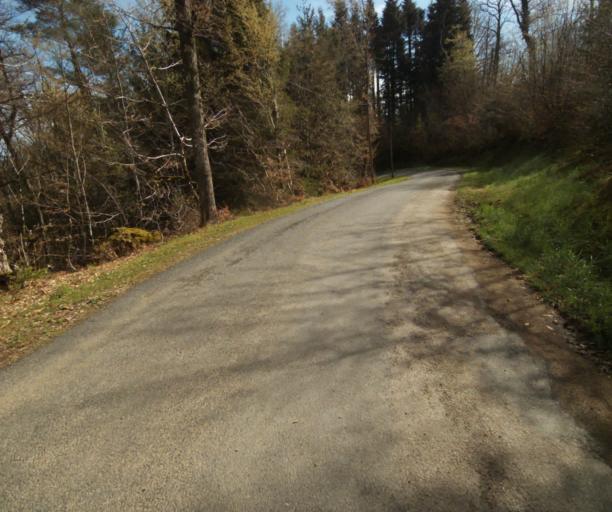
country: FR
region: Limousin
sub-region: Departement de la Correze
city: Laguenne
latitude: 45.2816
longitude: 1.8296
